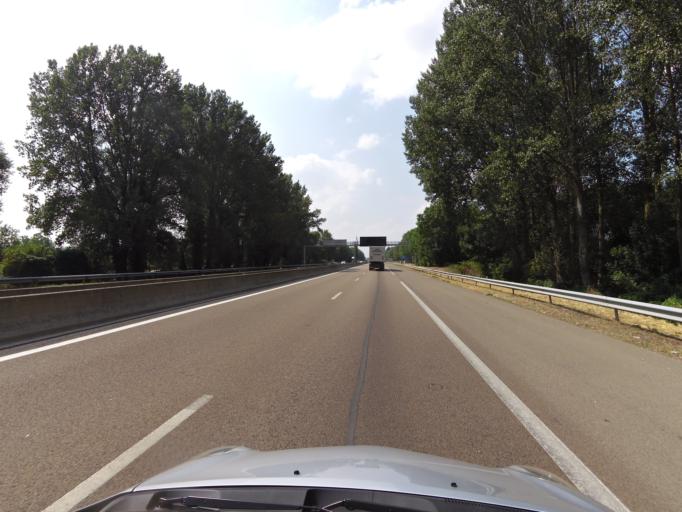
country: FR
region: Champagne-Ardenne
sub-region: Departement de la Marne
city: Reims
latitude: 49.2540
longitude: 4.0084
